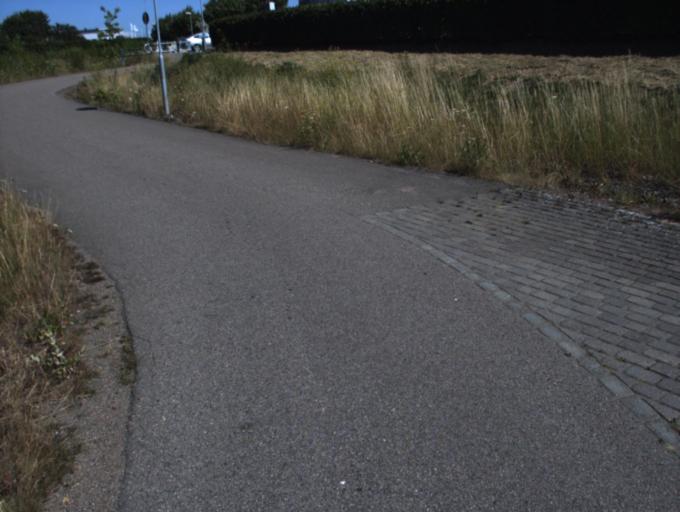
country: SE
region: Skane
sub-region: Helsingborg
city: Odakra
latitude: 56.0760
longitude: 12.7118
